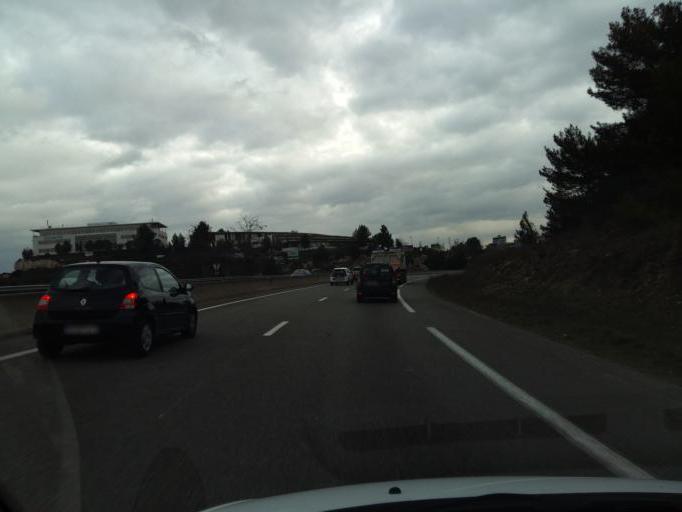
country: FR
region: Provence-Alpes-Cote d'Azur
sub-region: Departement des Bouches-du-Rhone
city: Cabries
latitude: 43.4844
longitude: 5.3559
